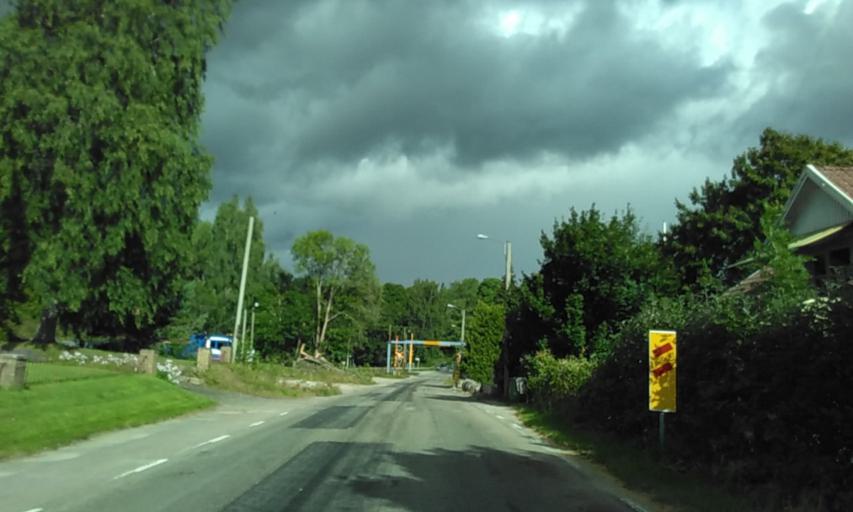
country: SE
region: Vaestra Goetaland
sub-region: Vargarda Kommun
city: Jonstorp
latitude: 58.0079
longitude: 12.7092
